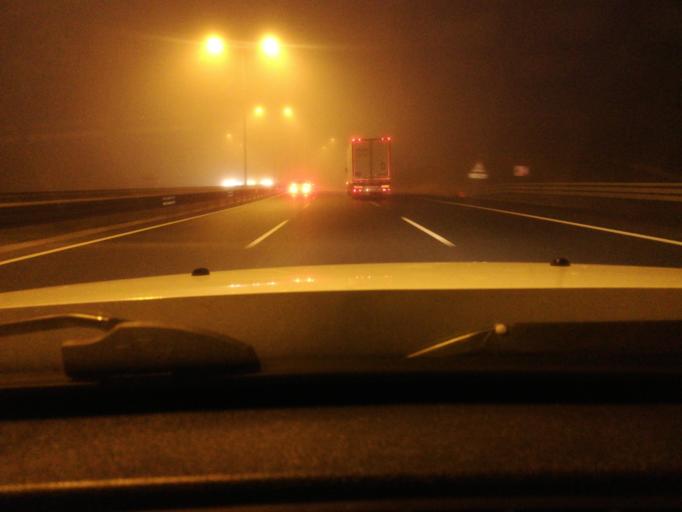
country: TR
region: Istanbul
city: Sultanbeyli
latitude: 40.9690
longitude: 29.3220
